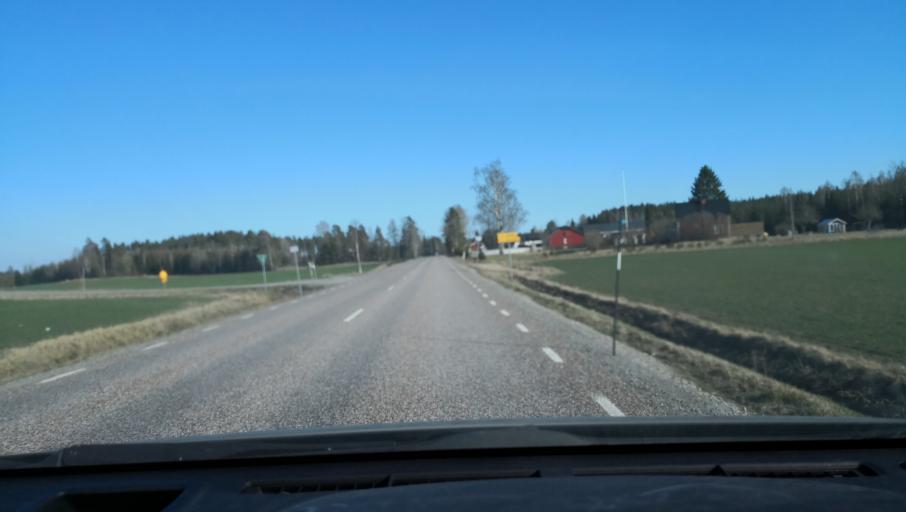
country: SE
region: Vaestmanland
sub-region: Vasteras
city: Skultuna
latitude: 59.8768
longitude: 16.3852
